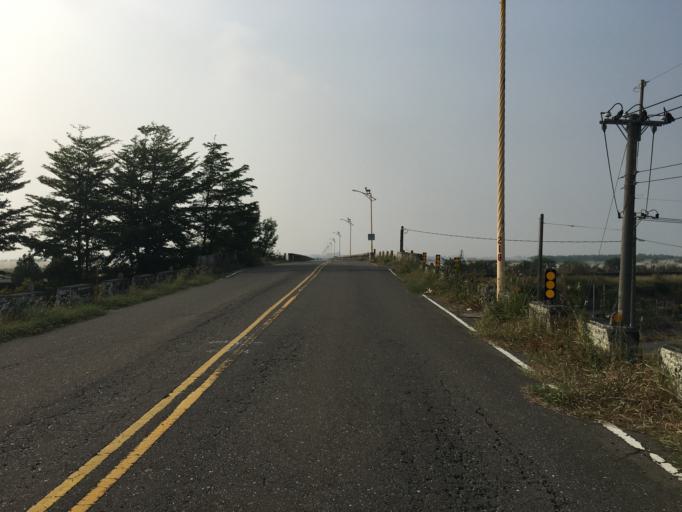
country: TW
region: Taiwan
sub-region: Chiayi
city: Taibao
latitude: 23.3979
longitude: 120.3341
